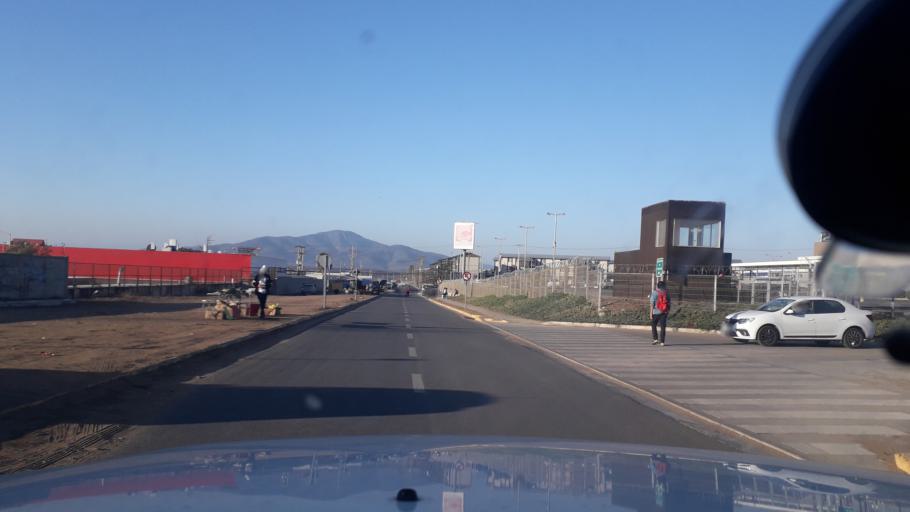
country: CL
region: Valparaiso
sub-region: Provincia de Valparaiso
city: Vina del Mar
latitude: -32.9314
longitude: -71.5196
